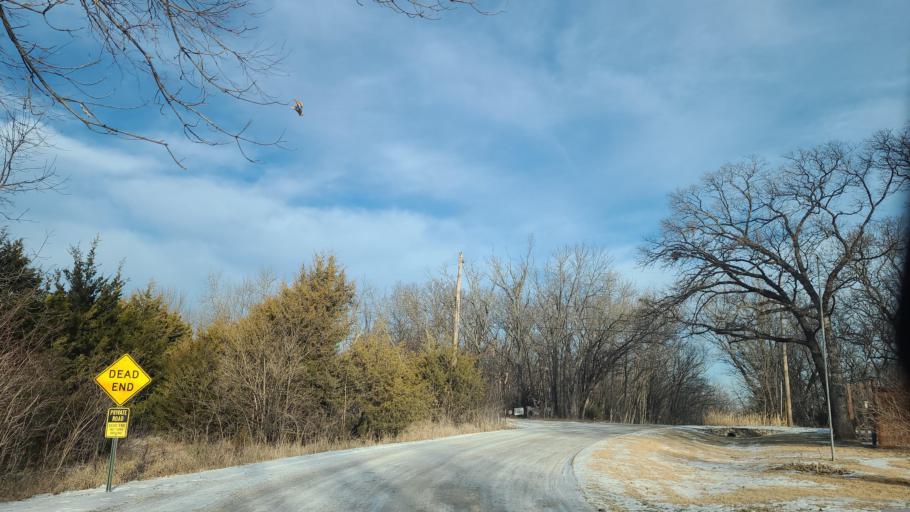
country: US
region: Kansas
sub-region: Douglas County
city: Lawrence
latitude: 38.9874
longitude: -95.2975
